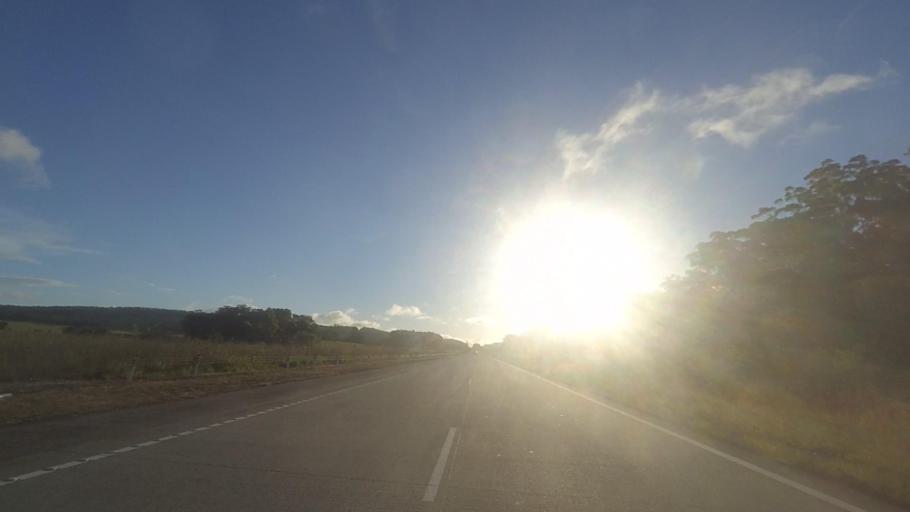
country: AU
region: New South Wales
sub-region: Great Lakes
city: Bulahdelah
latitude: -32.5231
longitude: 152.1998
